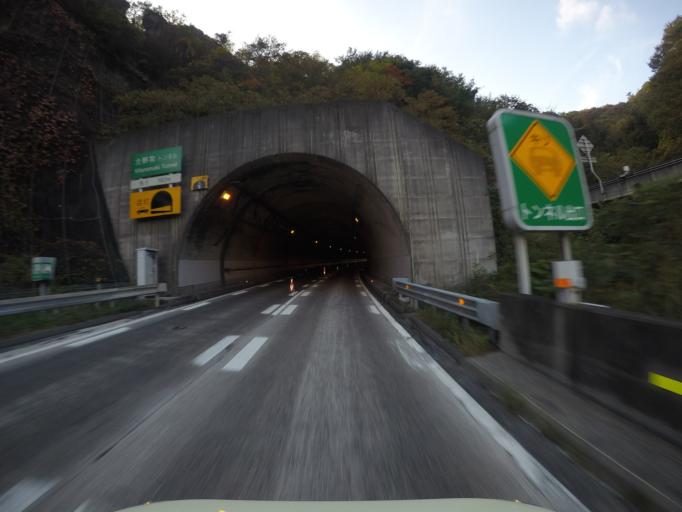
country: JP
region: Gunma
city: Annaka
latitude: 36.3079
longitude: 138.6831
